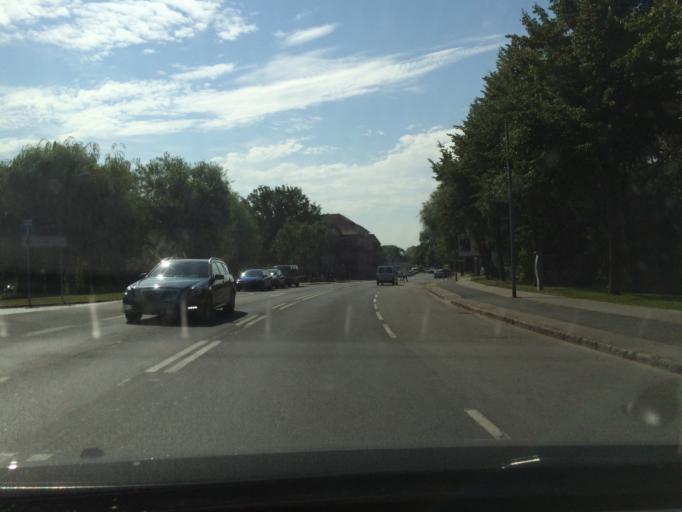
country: DE
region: Mecklenburg-Vorpommern
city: Stralsund
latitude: 54.3077
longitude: 13.0889
